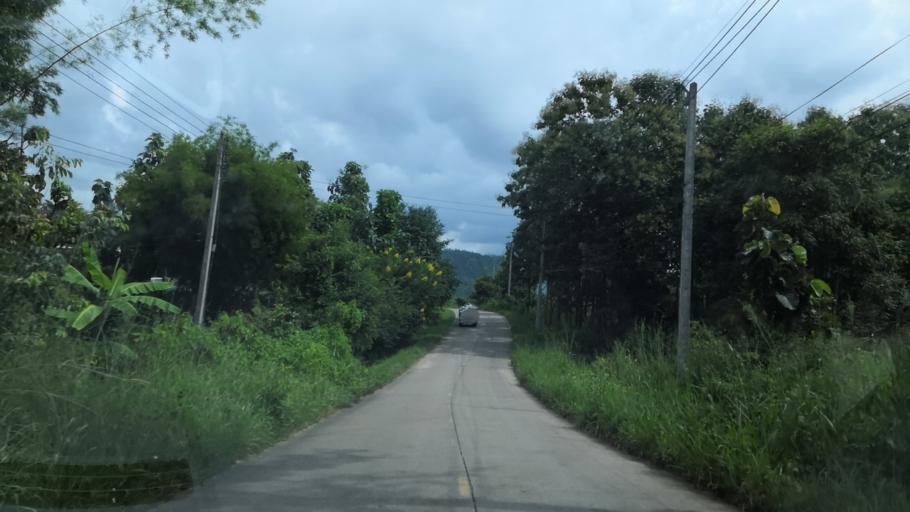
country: TH
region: Mae Hong Son
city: Khun Yuam
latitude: 18.8191
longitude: 97.9305
